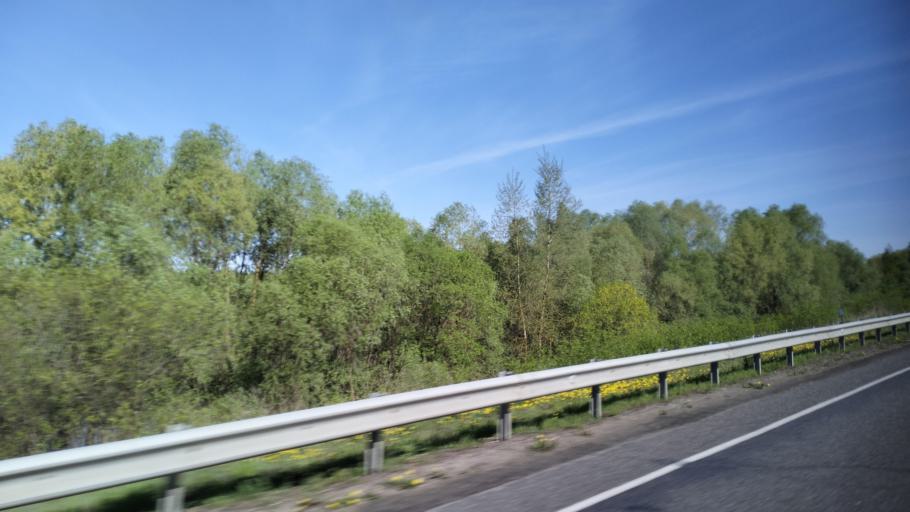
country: BY
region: Gomel
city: Turaw
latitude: 52.0924
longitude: 27.8291
